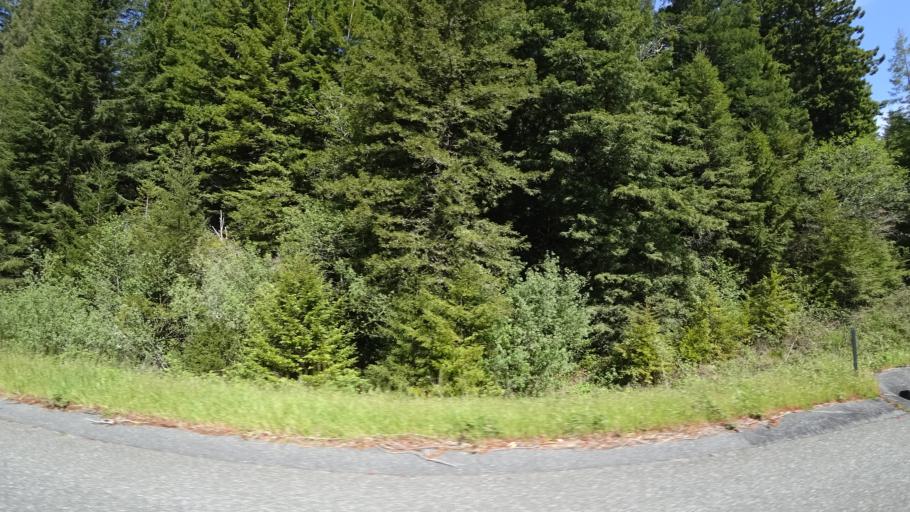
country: US
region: California
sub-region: Humboldt County
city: Westhaven-Moonstone
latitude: 41.3586
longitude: -124.0092
